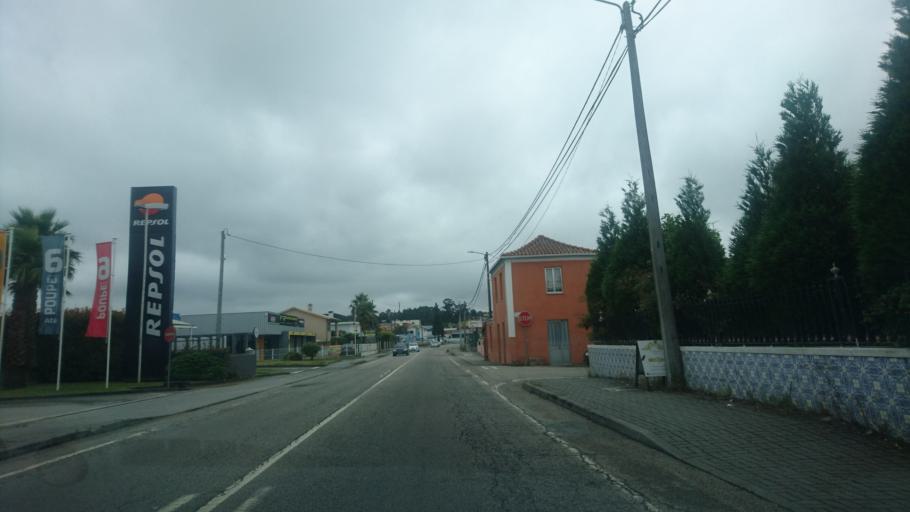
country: PT
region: Aveiro
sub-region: Santa Maria da Feira
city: Sao Joao de Ver
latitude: 40.9662
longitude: -8.5379
